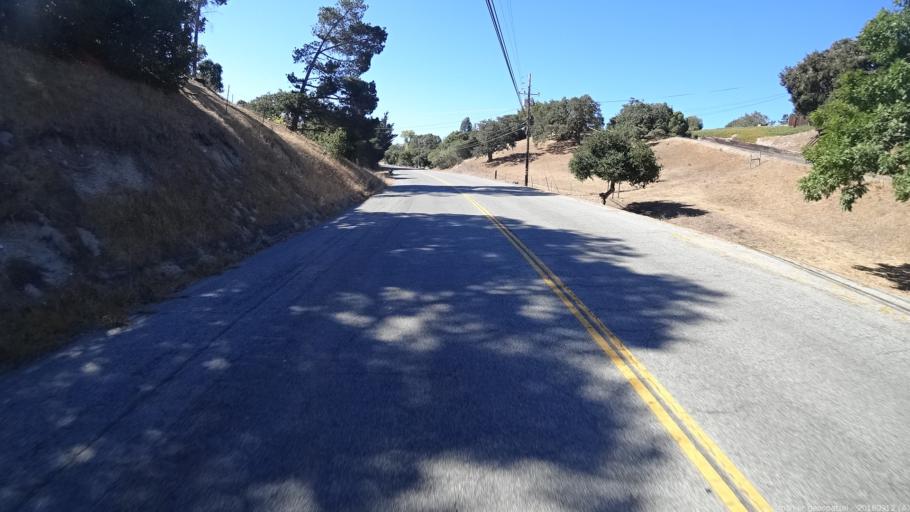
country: US
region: California
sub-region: Monterey County
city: Carmel Valley Village
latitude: 36.5725
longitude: -121.7305
